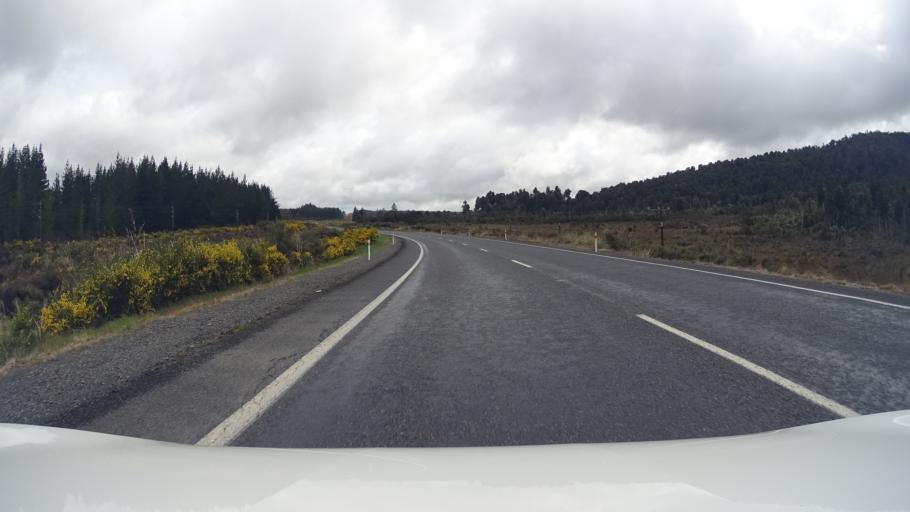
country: NZ
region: Manawatu-Wanganui
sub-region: Ruapehu District
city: Waiouru
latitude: -39.2213
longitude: 175.4004
